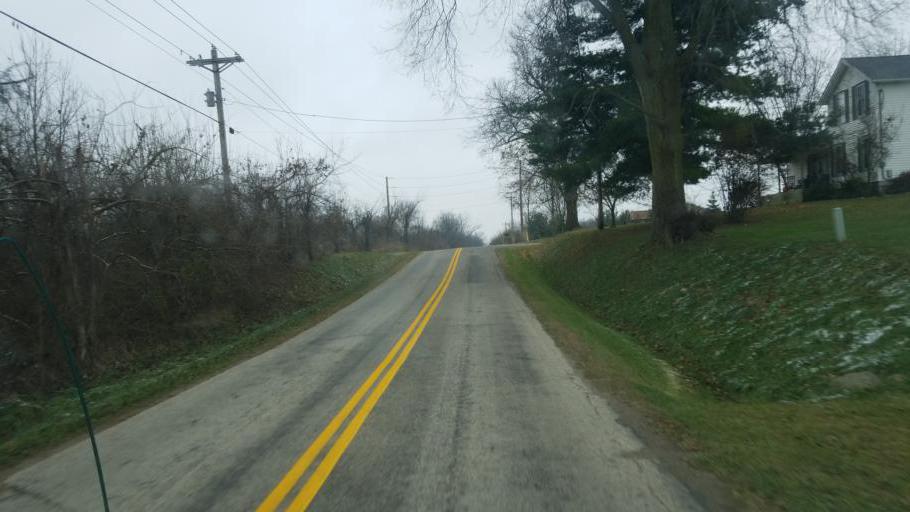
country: US
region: Ohio
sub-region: Huron County
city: New London
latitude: 41.0603
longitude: -82.3266
